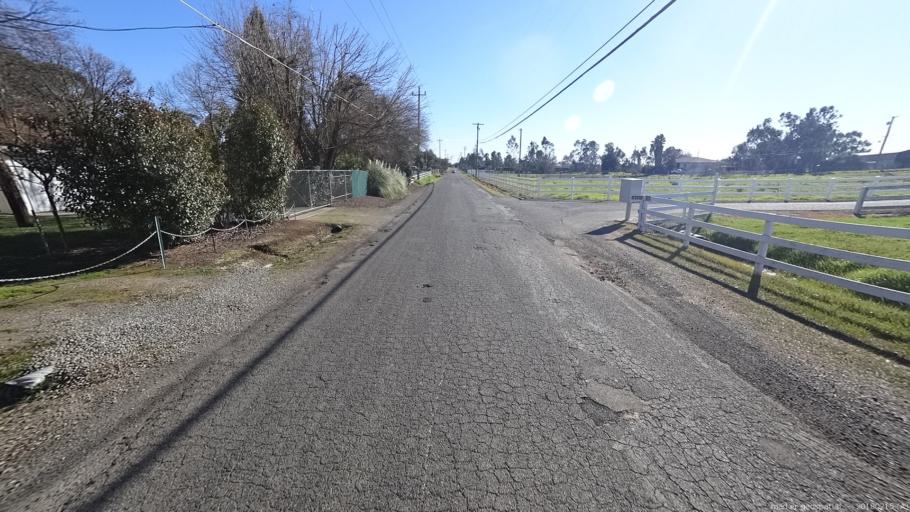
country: US
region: California
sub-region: Sacramento County
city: Rio Linda
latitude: 38.6803
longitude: -121.4754
